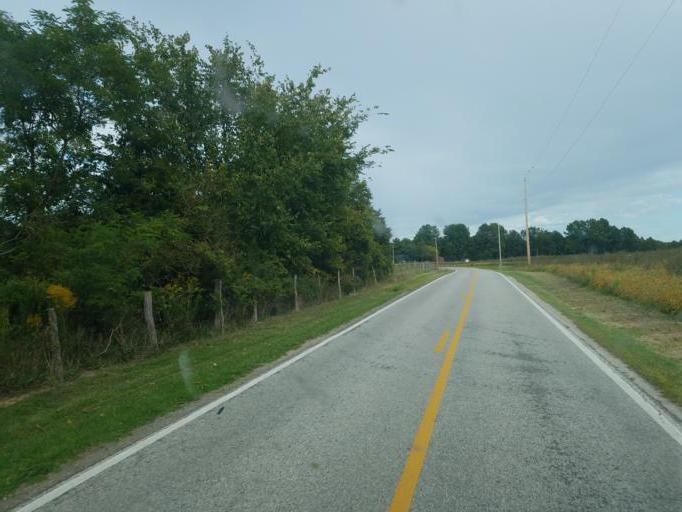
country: US
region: Ohio
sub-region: Knox County
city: Centerburg
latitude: 40.2861
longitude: -82.7784
